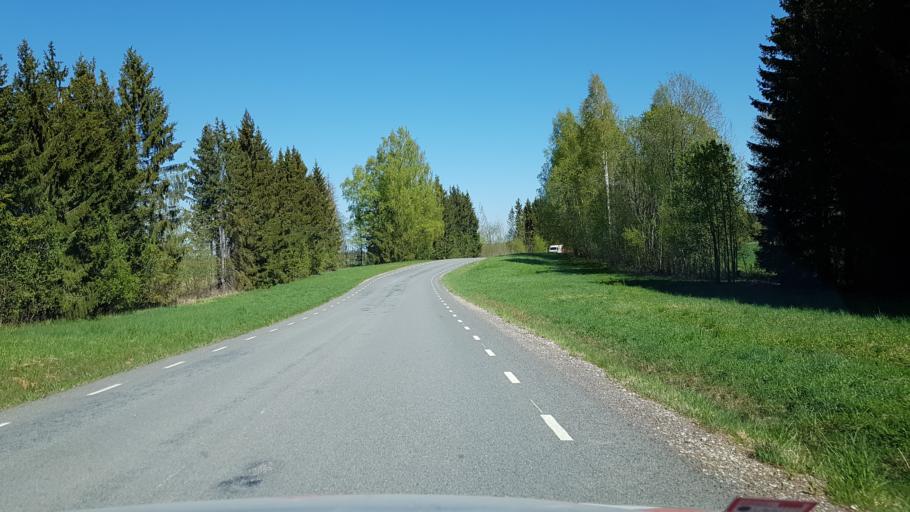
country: EE
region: Vorumaa
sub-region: Voru linn
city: Voru
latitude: 57.9494
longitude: 26.9557
